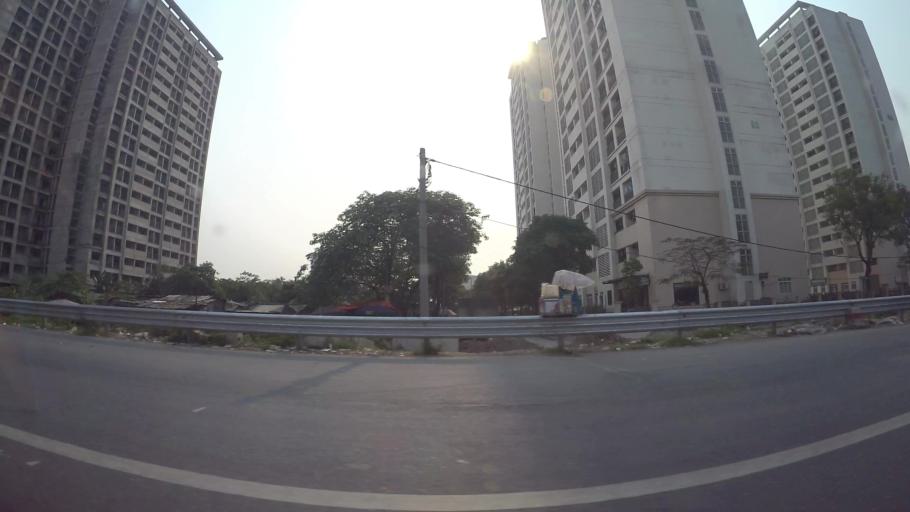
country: VN
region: Ha Noi
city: Van Dien
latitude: 20.9591
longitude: 105.8494
